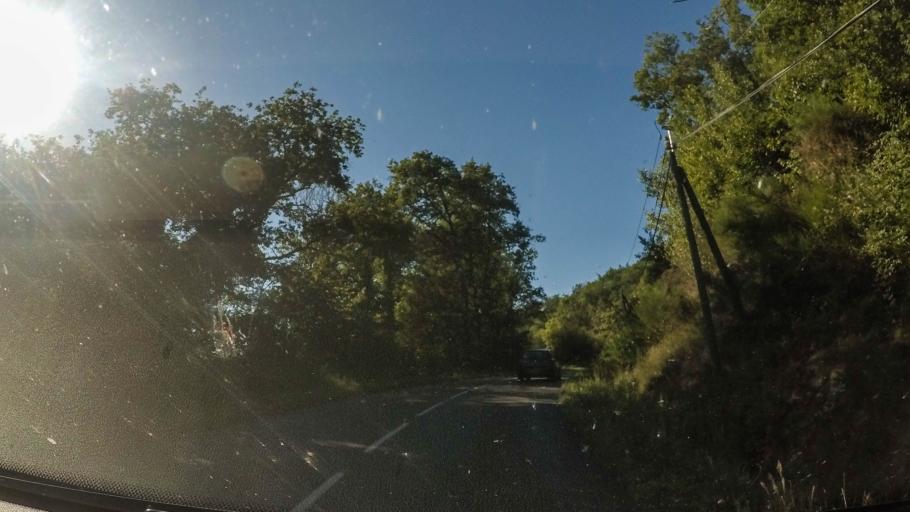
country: FR
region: Midi-Pyrenees
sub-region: Departement de l'Aveyron
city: Saint-Christophe-Vallon
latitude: 44.5519
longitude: 2.3967
